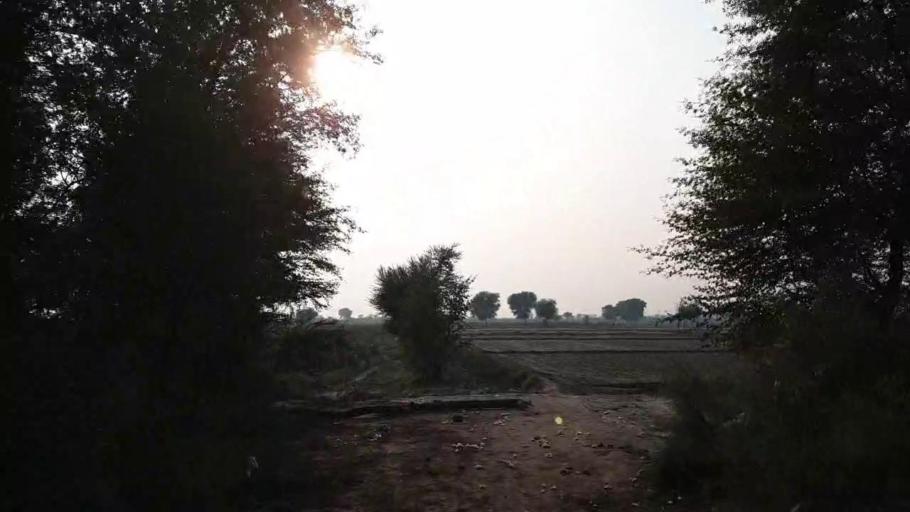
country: PK
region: Sindh
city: Bhan
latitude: 26.4914
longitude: 67.7706
